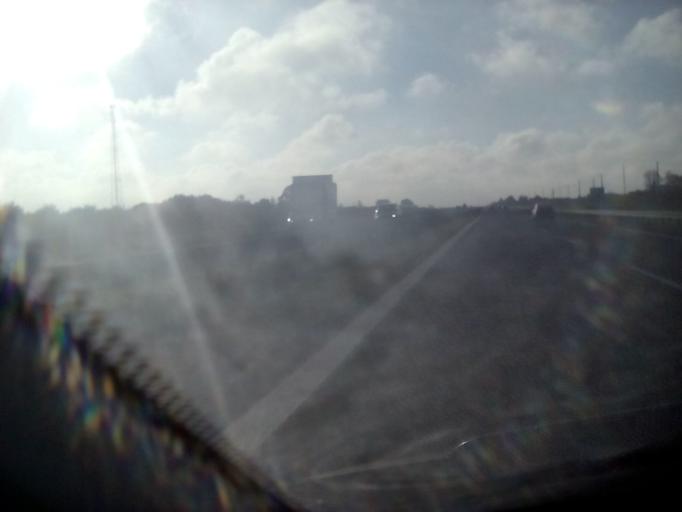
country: PL
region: Masovian Voivodeship
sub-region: Powiat grojecki
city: Jasieniec
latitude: 51.7796
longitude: 20.8963
